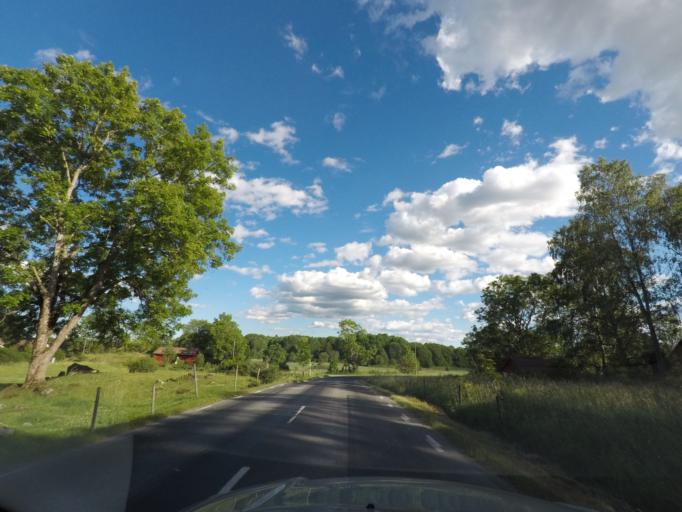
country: SE
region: Stockholm
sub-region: Sigtuna Kommun
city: Marsta
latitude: 59.7013
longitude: 17.9758
